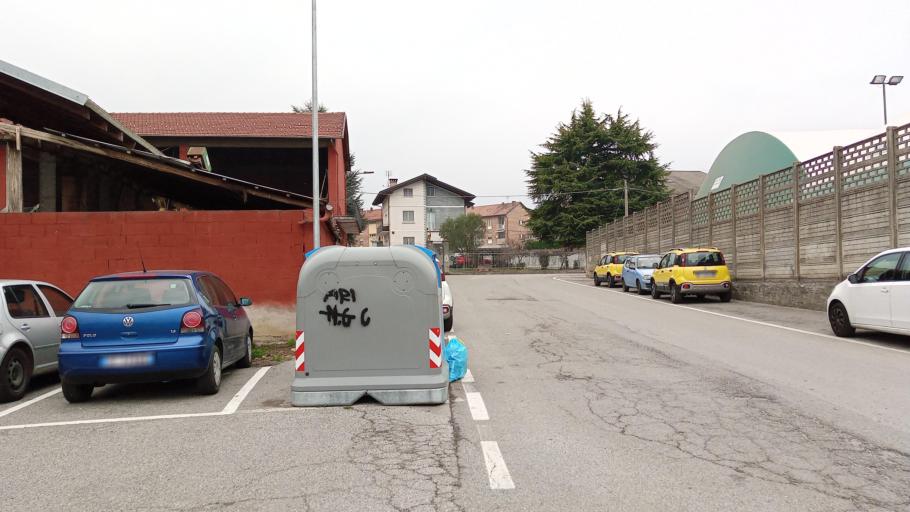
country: IT
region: Piedmont
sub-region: Provincia di Torino
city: Giaveno
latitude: 45.0460
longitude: 7.3510
